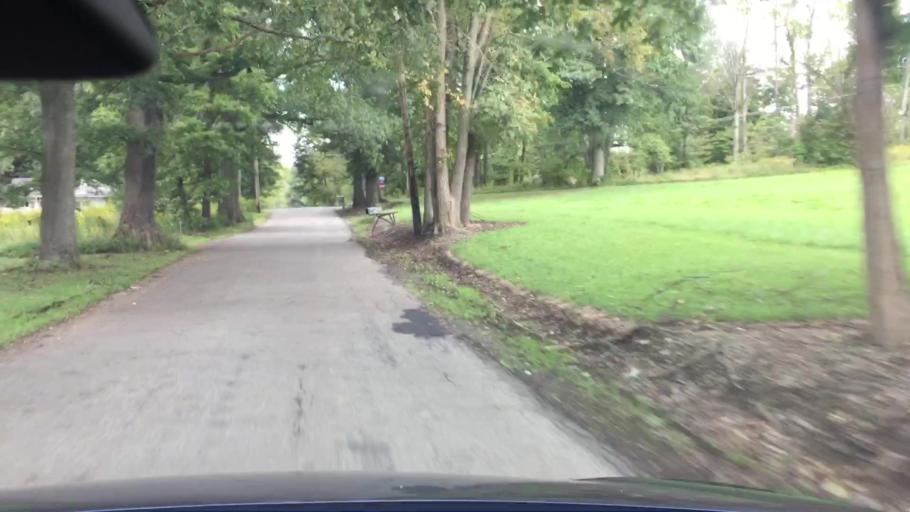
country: US
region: Pennsylvania
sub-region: Butler County
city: Nixon
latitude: 40.7447
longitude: -79.8846
